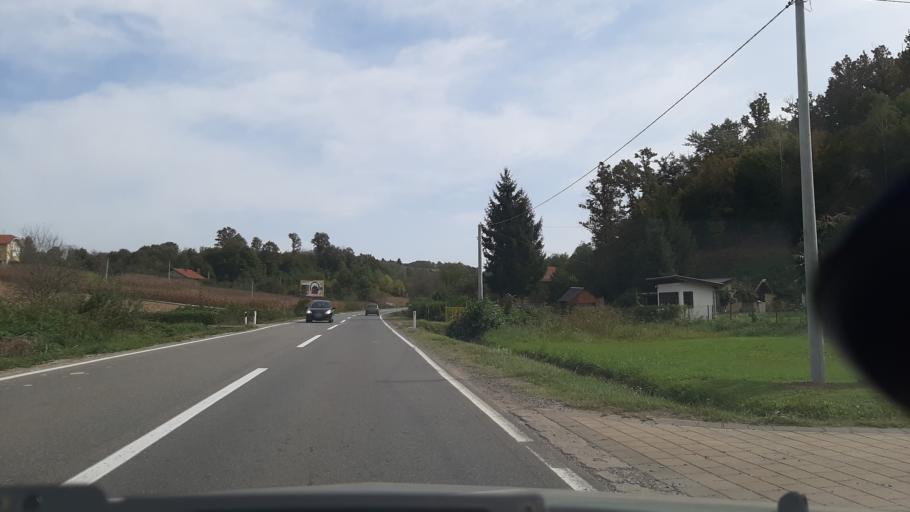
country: BA
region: Republika Srpska
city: Laktasi
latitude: 44.8748
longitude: 17.3222
